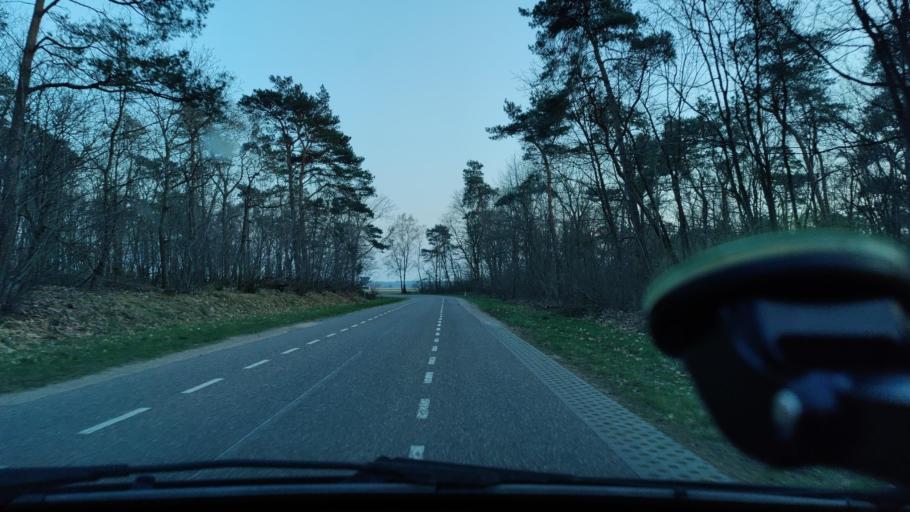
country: NL
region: Limburg
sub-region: Gemeente Bergen
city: Wellerlooi
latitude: 51.5809
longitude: 6.1213
